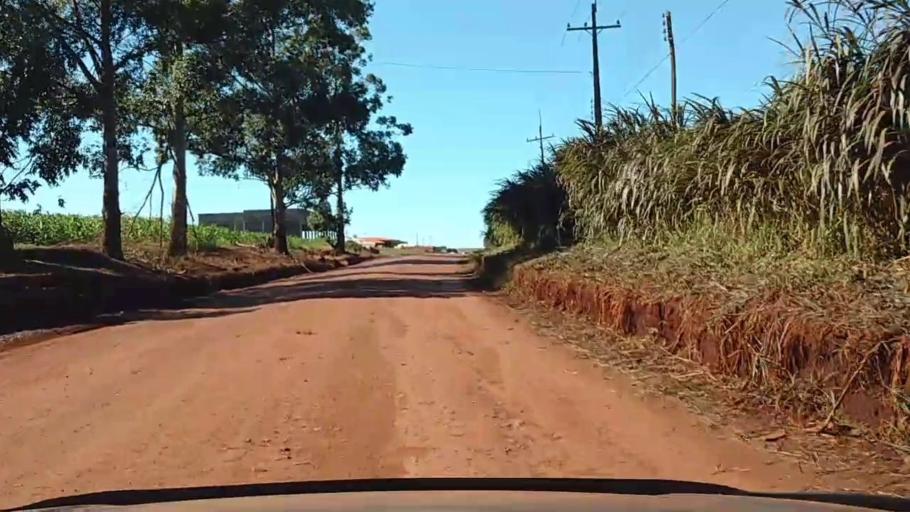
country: PY
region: Alto Parana
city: Naranjal
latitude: -25.8969
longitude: -55.4587
